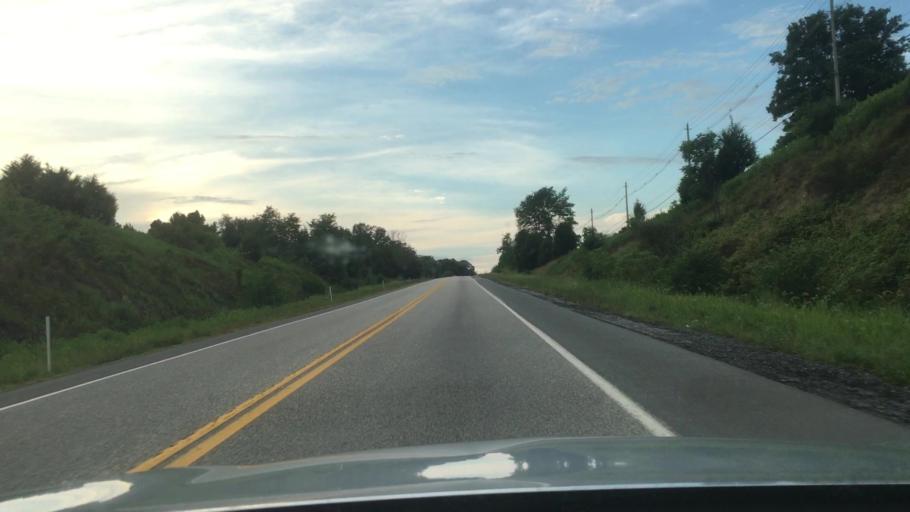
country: US
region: Pennsylvania
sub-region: York County
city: Dover
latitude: 40.0679
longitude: -76.9210
